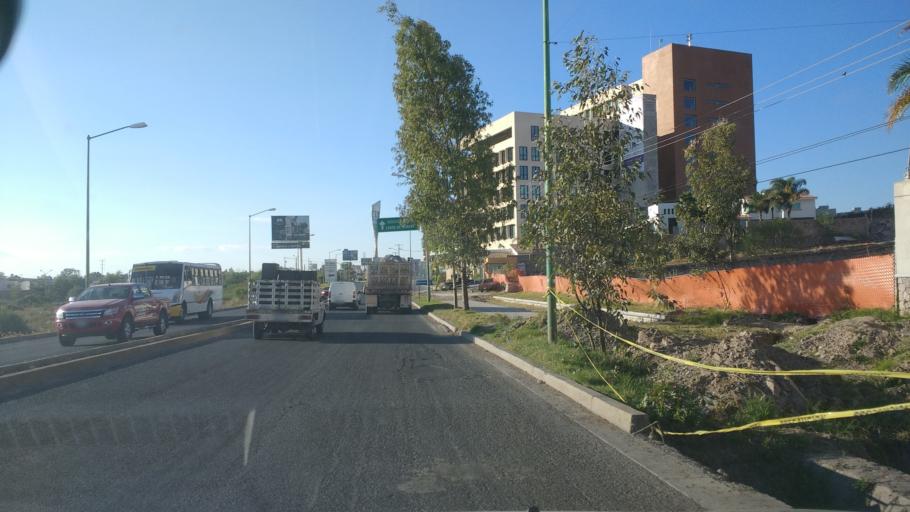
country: MX
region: Guanajuato
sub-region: Leon
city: La Ermita
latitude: 21.1696
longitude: -101.7317
